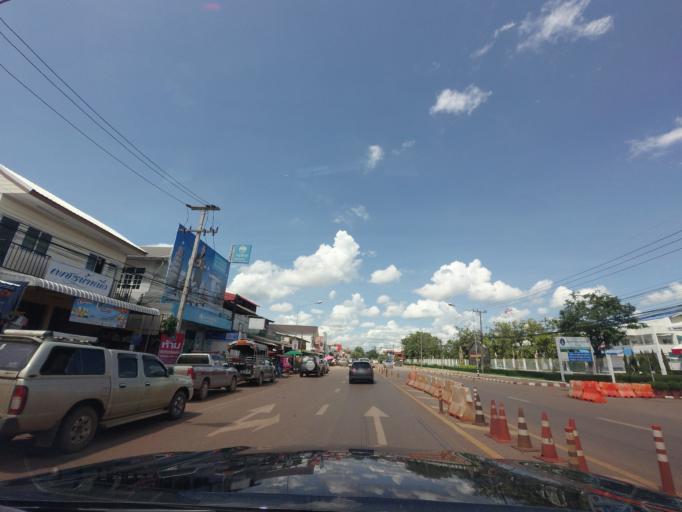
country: TH
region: Changwat Udon Thani
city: Ban Dung
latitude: 17.6917
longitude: 103.2576
